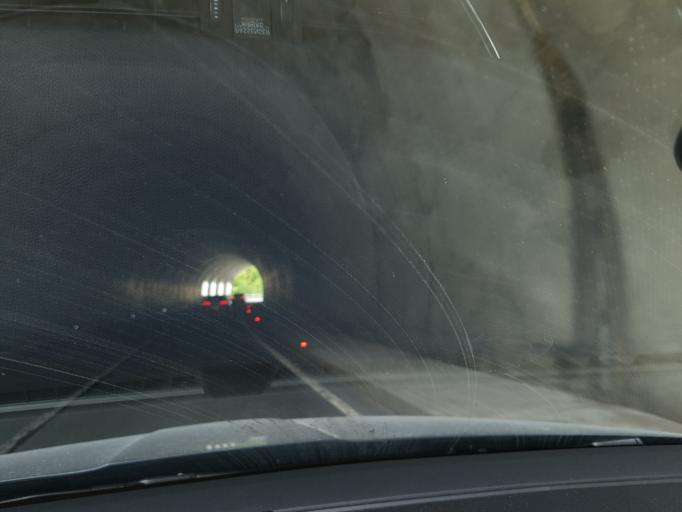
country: AT
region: Salzburg
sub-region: Politischer Bezirk Sankt Johann im Pongau
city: Sankt Johann im Pongau
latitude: 47.3025
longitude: 13.2039
